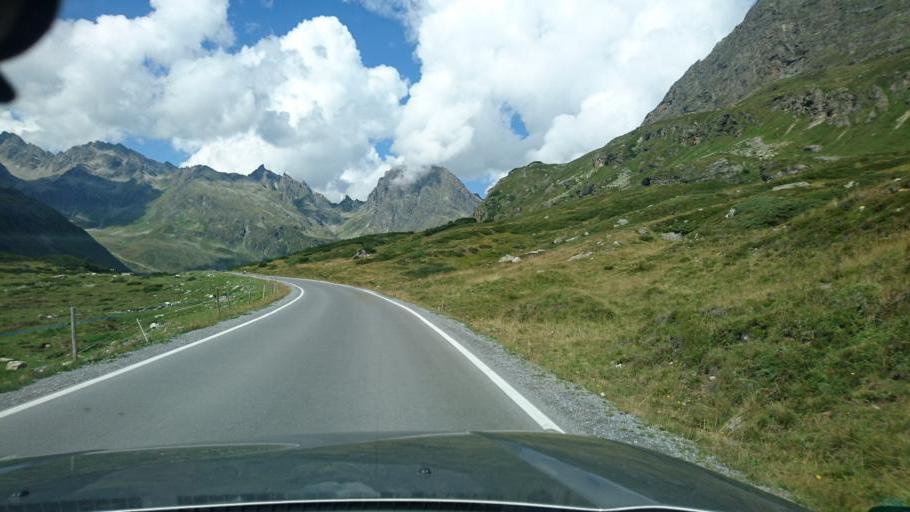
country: AT
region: Vorarlberg
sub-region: Politischer Bezirk Bludenz
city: Gaschurn
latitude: 46.9198
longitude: 10.0823
